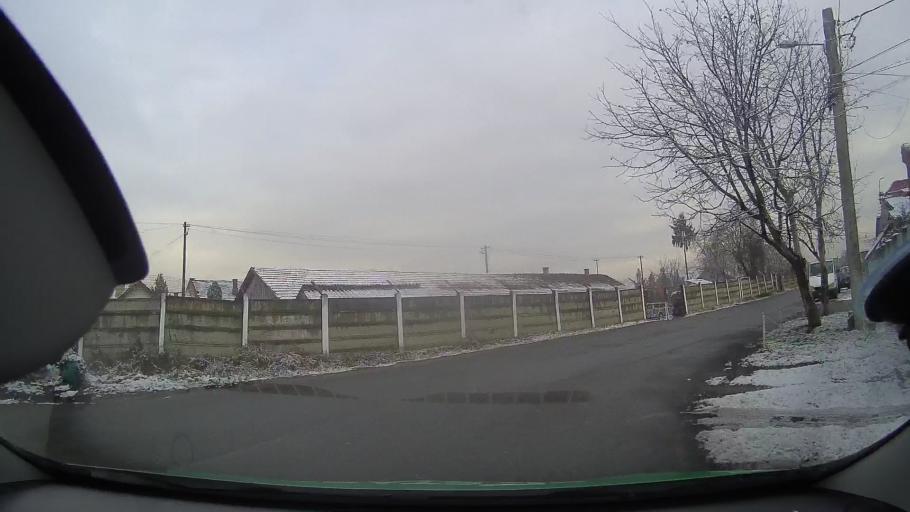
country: RO
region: Mures
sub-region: Comuna Ludus
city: Ludus
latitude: 46.4658
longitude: 24.0862
